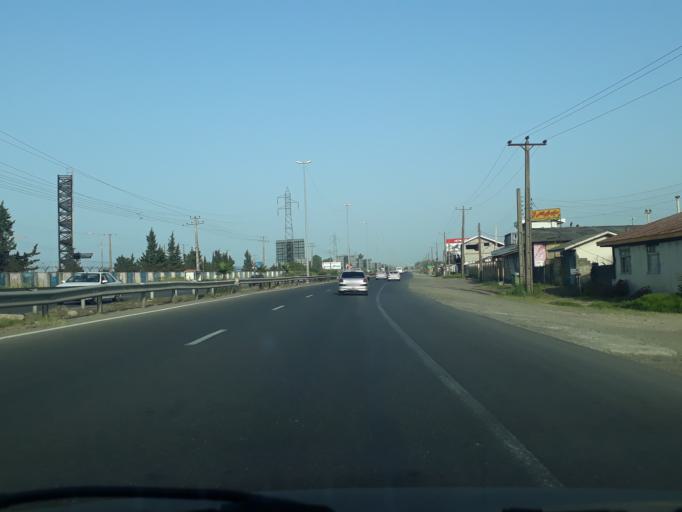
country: IR
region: Gilan
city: Bandar-e Anzali
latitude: 37.4601
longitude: 49.5888
